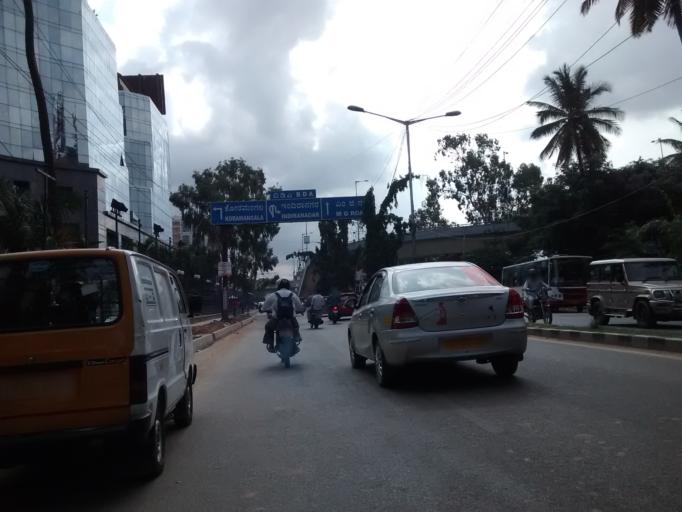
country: IN
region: Karnataka
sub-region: Bangalore Urban
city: Bangalore
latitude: 12.9603
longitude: 77.6439
